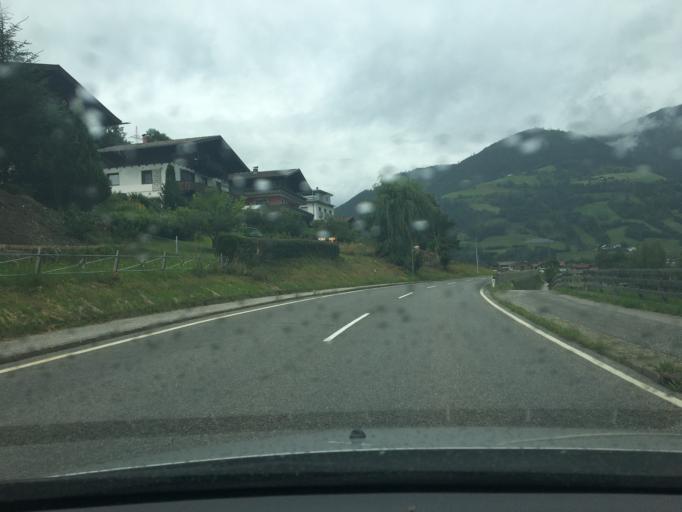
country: AT
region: Salzburg
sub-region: Politischer Bezirk Zell am See
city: Bruck an der Grossglocknerstrasse
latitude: 47.2733
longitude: 12.8259
